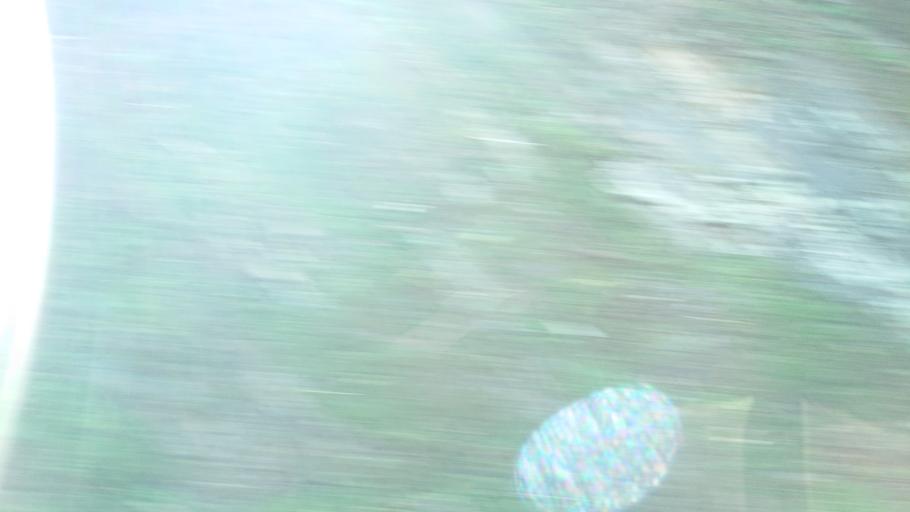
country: TW
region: Taiwan
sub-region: Yilan
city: Yilan
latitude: 24.5782
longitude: 121.4893
